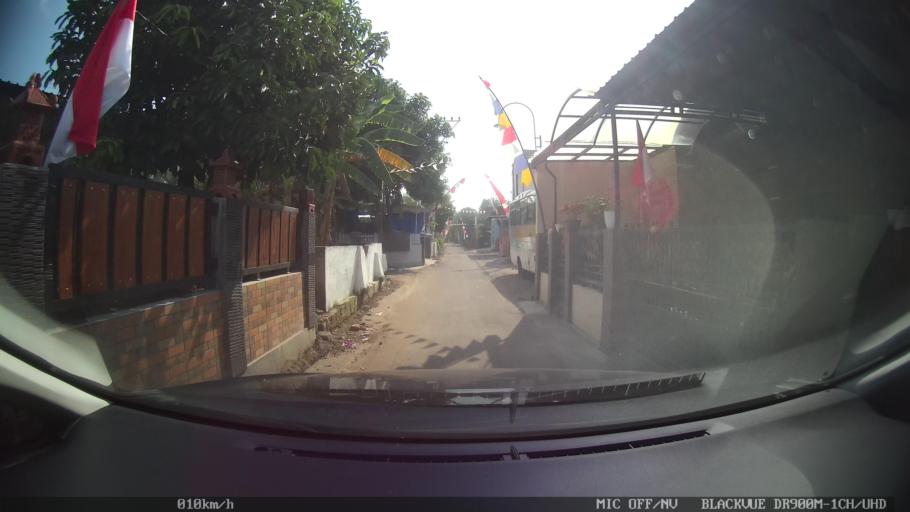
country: ID
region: Daerah Istimewa Yogyakarta
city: Sewon
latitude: -7.8340
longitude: 110.4044
